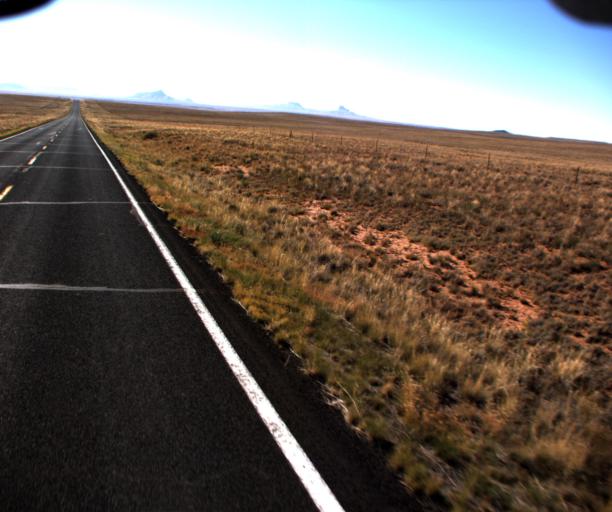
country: US
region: Arizona
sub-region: Navajo County
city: First Mesa
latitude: 35.6287
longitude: -110.4813
